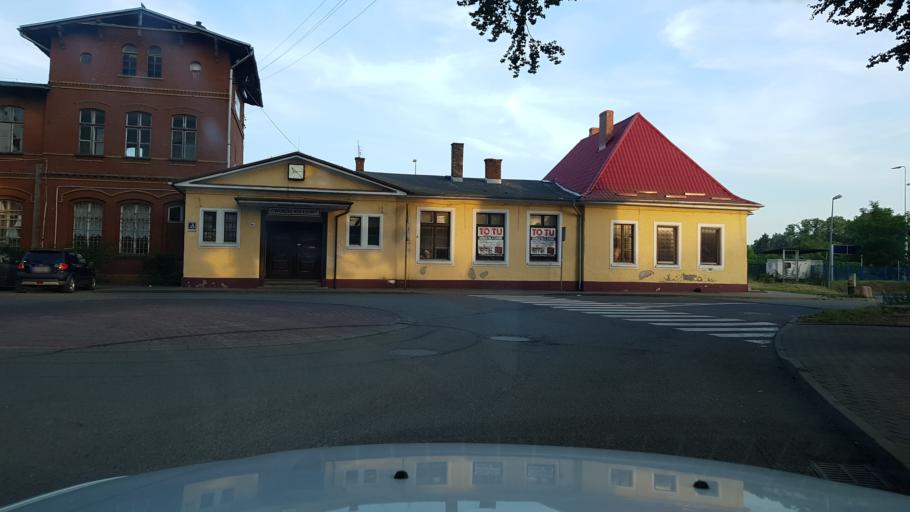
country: PL
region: West Pomeranian Voivodeship
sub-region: Powiat goleniowski
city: Nowogard
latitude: 53.6666
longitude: 15.1206
